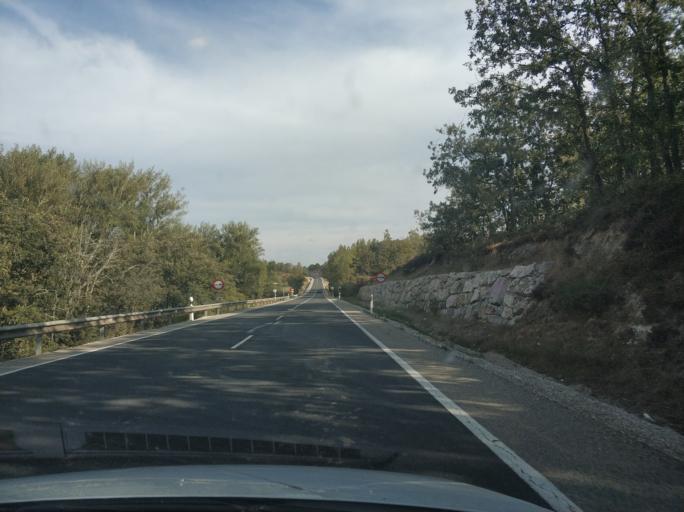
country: ES
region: Castille and Leon
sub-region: Provincia de Burgos
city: Basconcillos del Tozo
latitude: 42.7141
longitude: -4.0178
